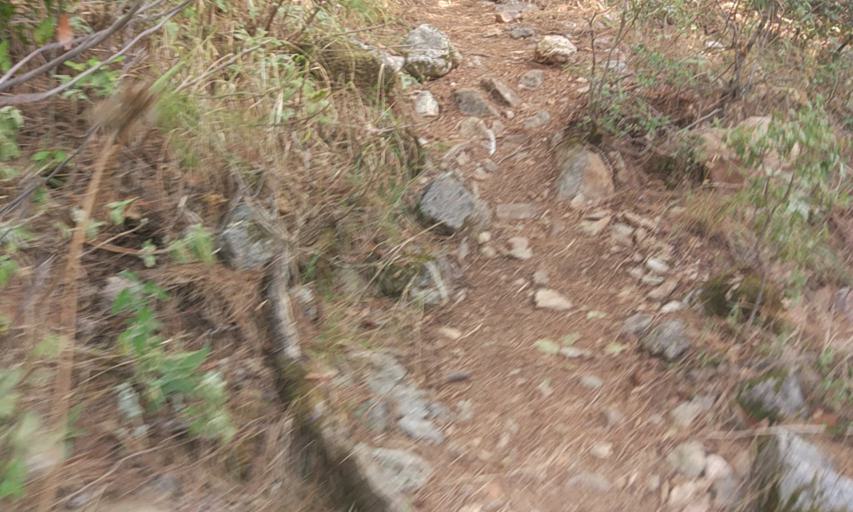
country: TR
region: Antalya
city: Tekirova
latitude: 36.3809
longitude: 30.4761
